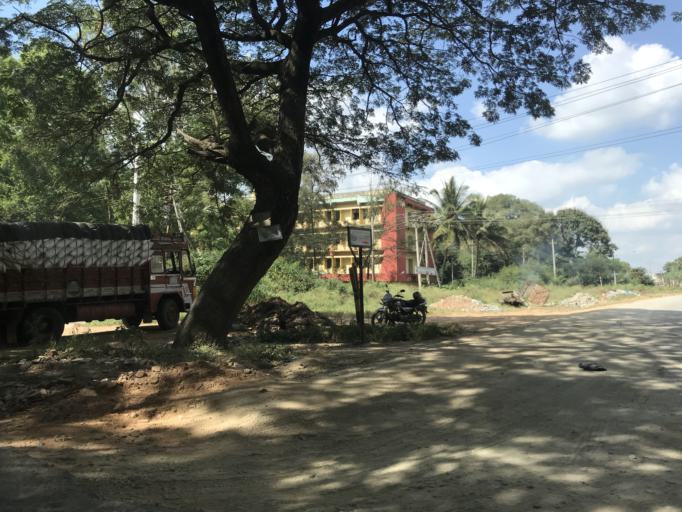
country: IN
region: Karnataka
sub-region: Hassan
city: Hassan
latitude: 12.9938
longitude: 76.0708
